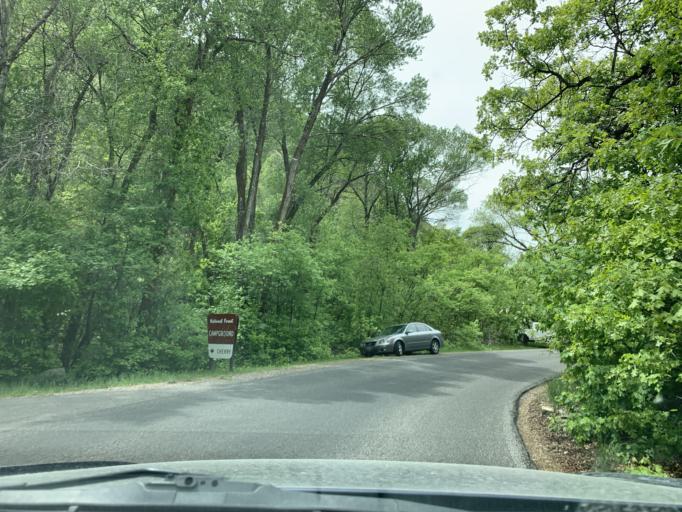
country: US
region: Utah
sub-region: Utah County
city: Mapleton
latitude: 40.1689
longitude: -111.4770
